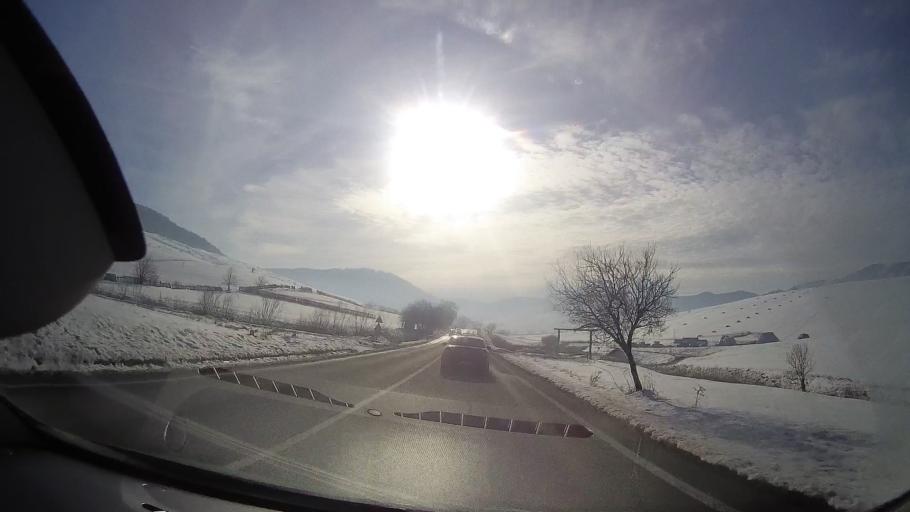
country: RO
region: Neamt
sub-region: Comuna Garcina
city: Garcina
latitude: 46.9905
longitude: 26.3621
